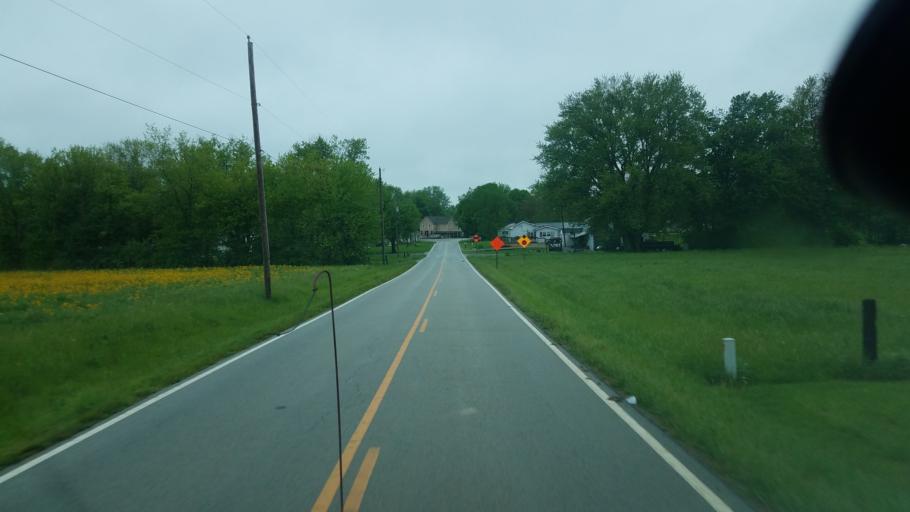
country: US
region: Ohio
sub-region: Highland County
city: Leesburg
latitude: 39.2857
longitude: -83.5888
